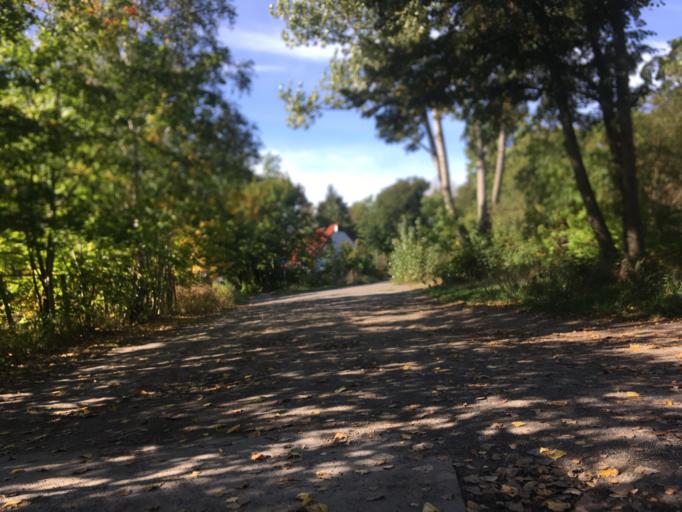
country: DE
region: Berlin
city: Altglienicke
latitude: 52.4093
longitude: 13.5529
